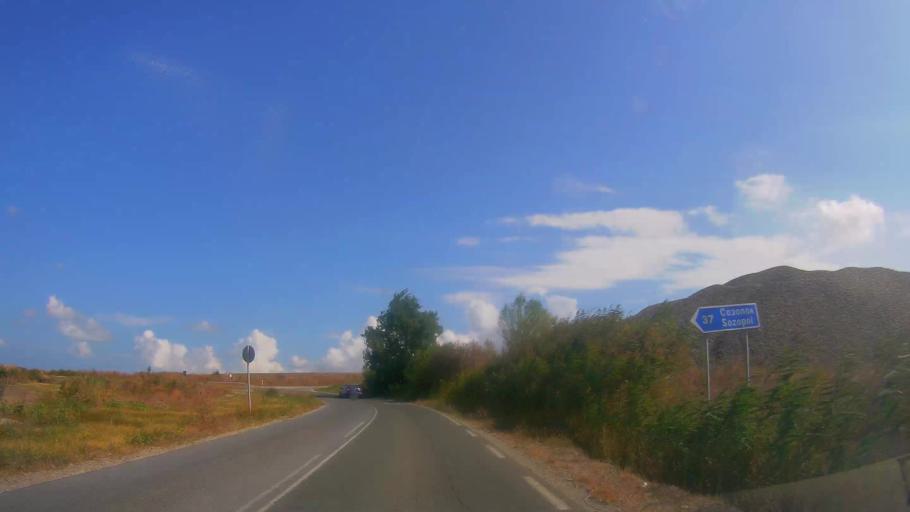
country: BG
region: Burgas
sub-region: Obshtina Burgas
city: Burgas
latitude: 42.4739
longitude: 27.3615
